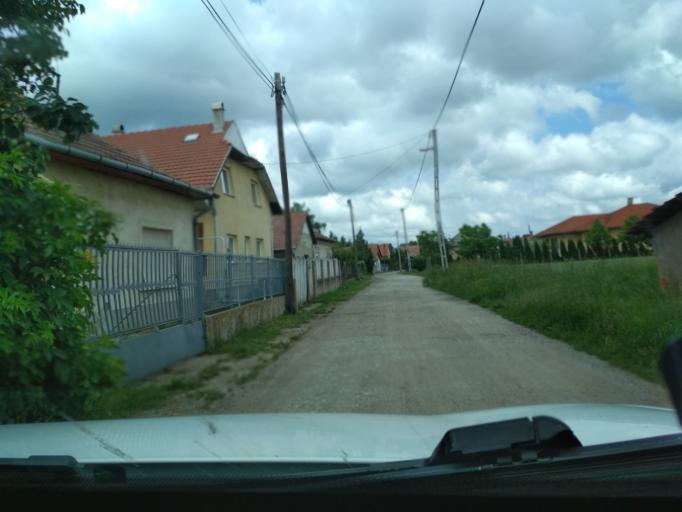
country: HU
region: Jasz-Nagykun-Szolnok
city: Tiszafured
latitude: 47.6136
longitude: 20.7398
